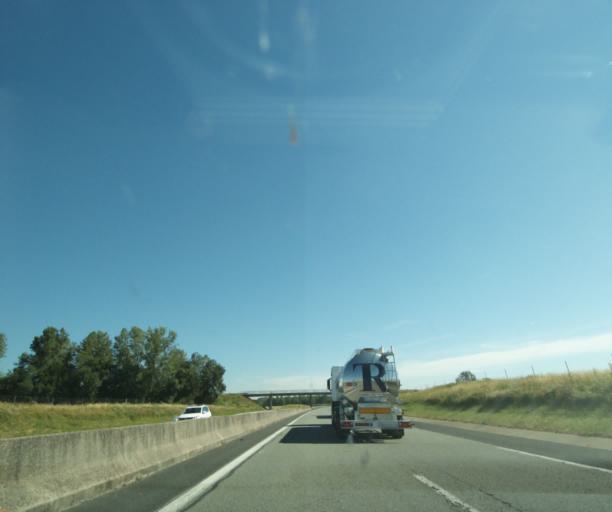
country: FR
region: Lorraine
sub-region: Departement des Vosges
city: Lamarche
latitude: 48.1254
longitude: 5.6657
